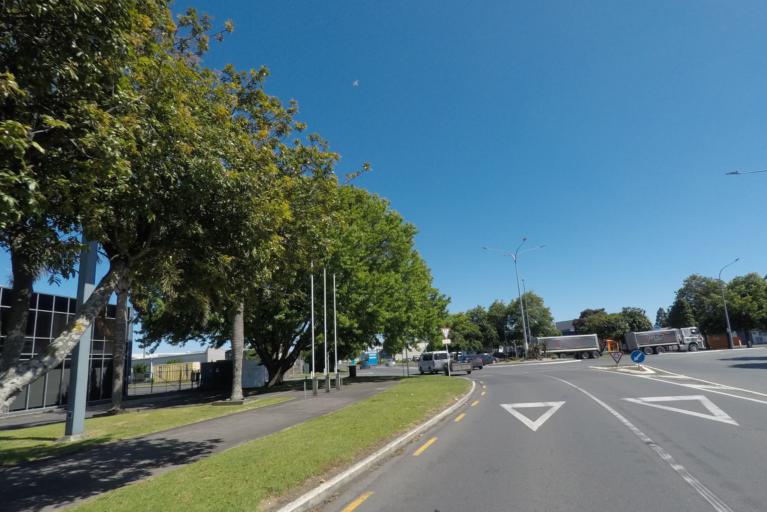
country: NZ
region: Auckland
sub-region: Auckland
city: Rosebank
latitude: -36.8730
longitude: 174.6695
